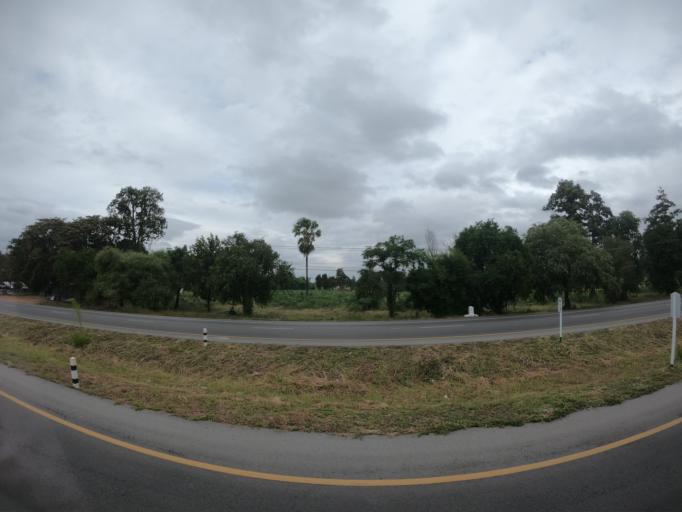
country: TH
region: Khon Kaen
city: Ban Phai
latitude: 16.0444
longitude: 102.8550
